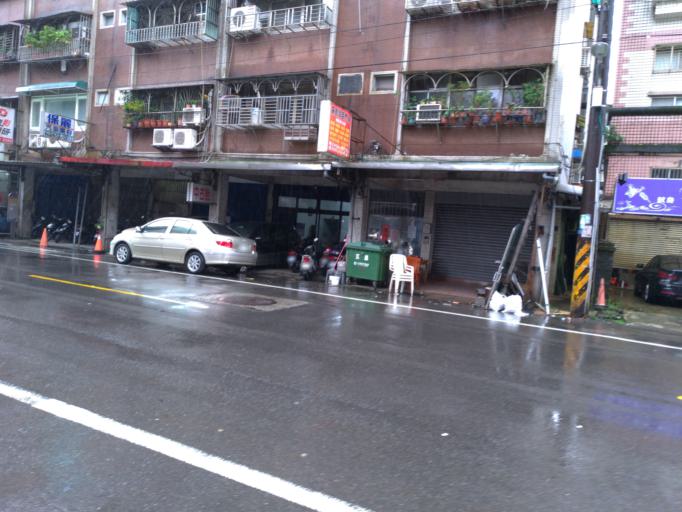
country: TW
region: Taiwan
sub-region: Keelung
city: Keelung
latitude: 25.0877
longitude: 121.6978
